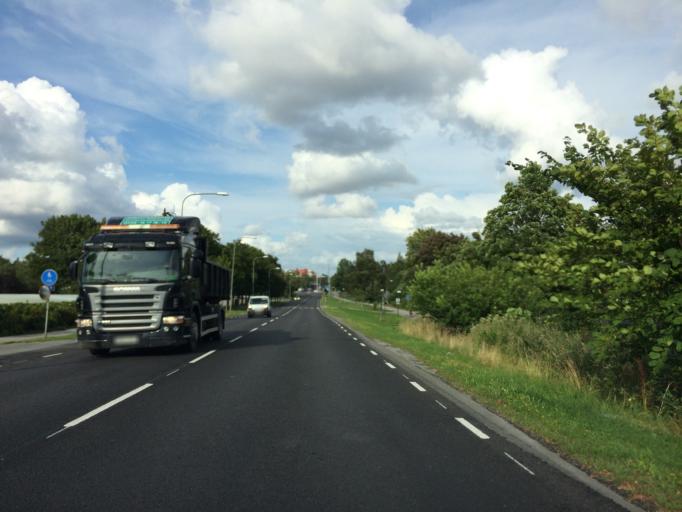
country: SE
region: Stockholm
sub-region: Huddinge Kommun
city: Segeltorp
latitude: 59.2857
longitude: 17.9774
